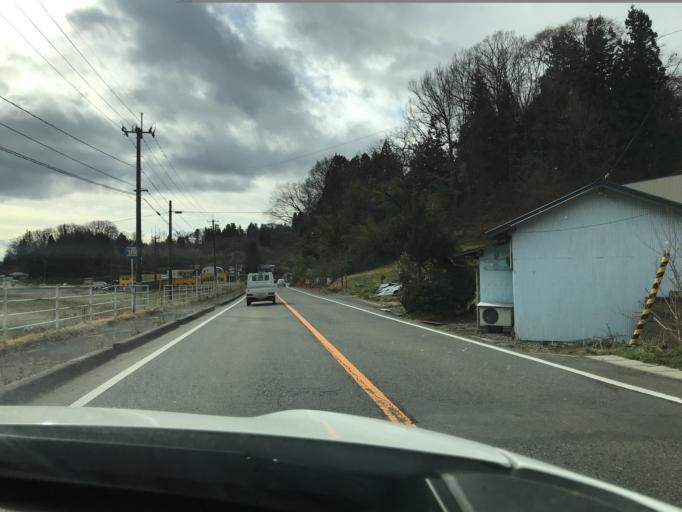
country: JP
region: Fukushima
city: Funehikimachi-funehiki
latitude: 37.5887
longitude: 140.5774
